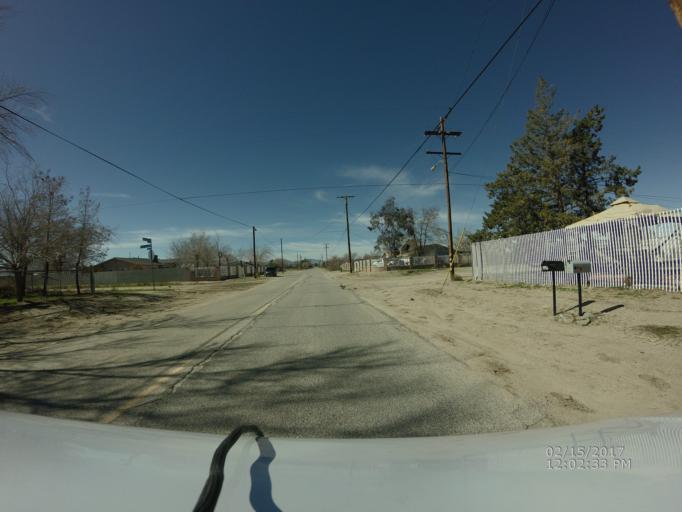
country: US
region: California
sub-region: Los Angeles County
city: Littlerock
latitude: 34.5743
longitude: -117.9562
